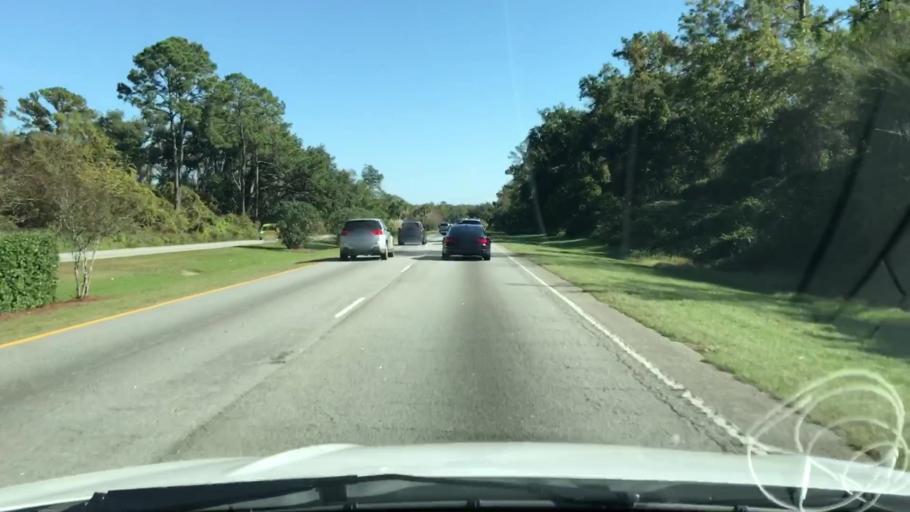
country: US
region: South Carolina
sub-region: Beaufort County
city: Hilton Head Island
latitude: 32.2181
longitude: -80.7668
